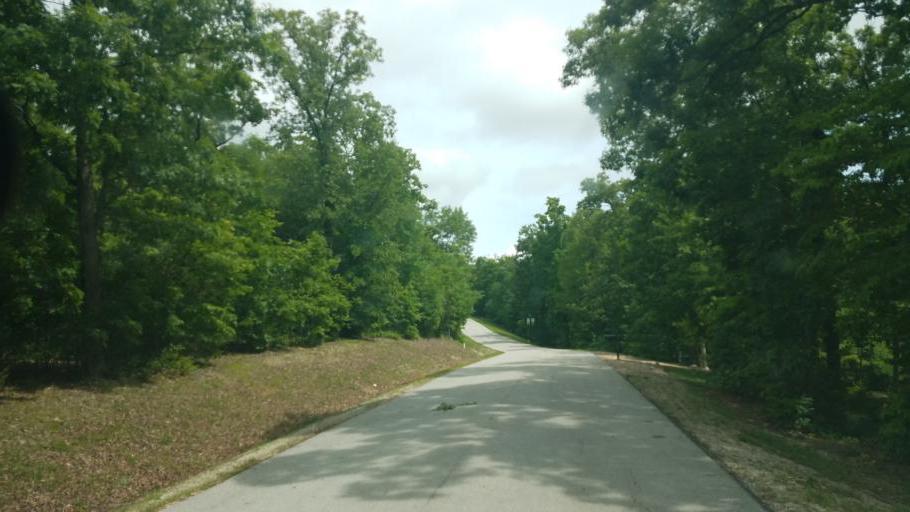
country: US
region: Missouri
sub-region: Camden County
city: Osage Beach
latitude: 38.1537
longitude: -92.6819
